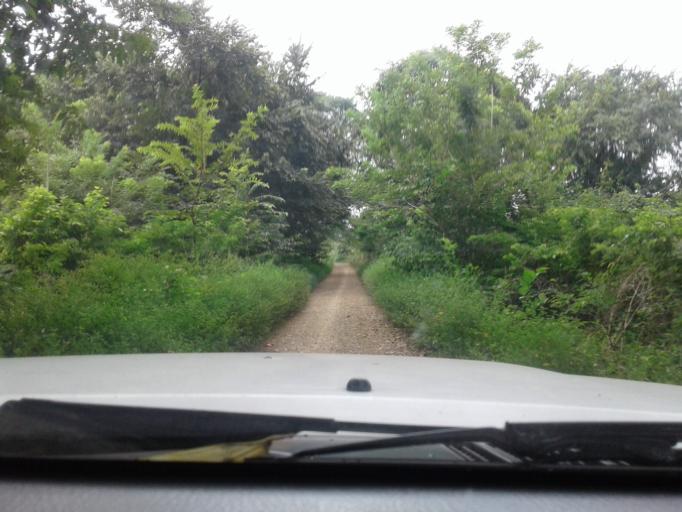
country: NI
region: Rivas
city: San Juan del Sur
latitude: 11.2273
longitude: -85.7854
